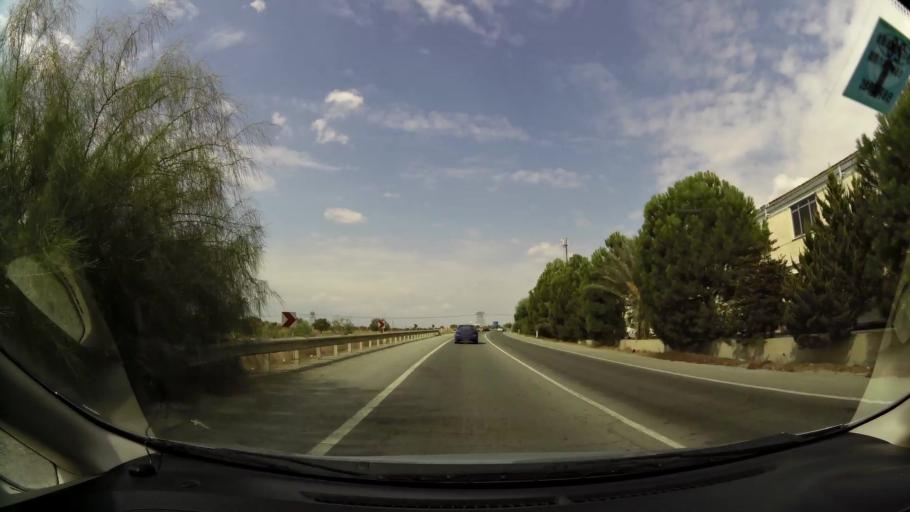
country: CY
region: Lefkosia
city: Tseri
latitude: 35.0615
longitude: 33.3471
